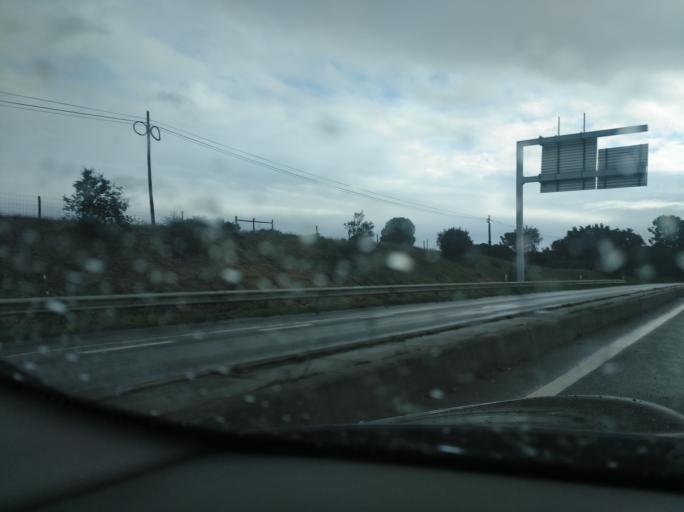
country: PT
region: Setubal
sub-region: Grandola
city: Grandola
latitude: 38.1093
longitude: -8.4183
